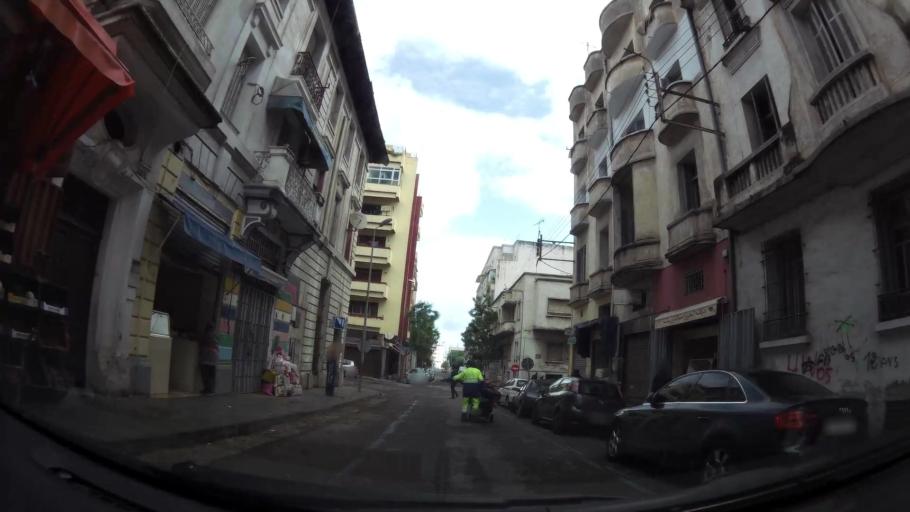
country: MA
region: Grand Casablanca
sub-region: Casablanca
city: Casablanca
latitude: 33.5940
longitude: -7.6070
